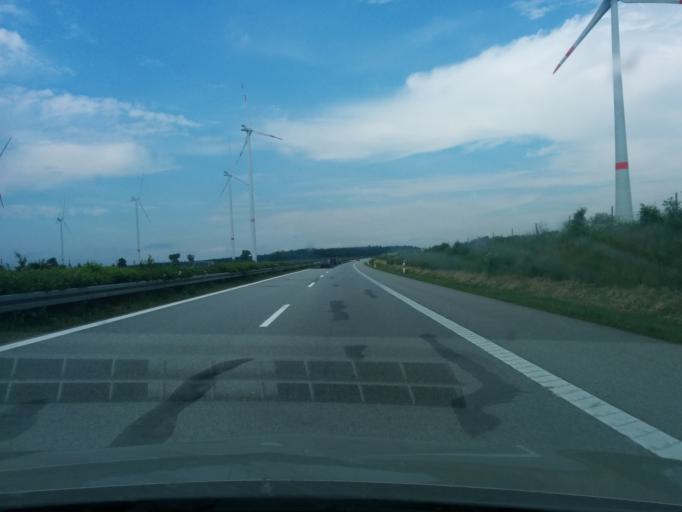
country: DE
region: Mecklenburg-Vorpommern
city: Jarmen
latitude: 53.8849
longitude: 13.3439
